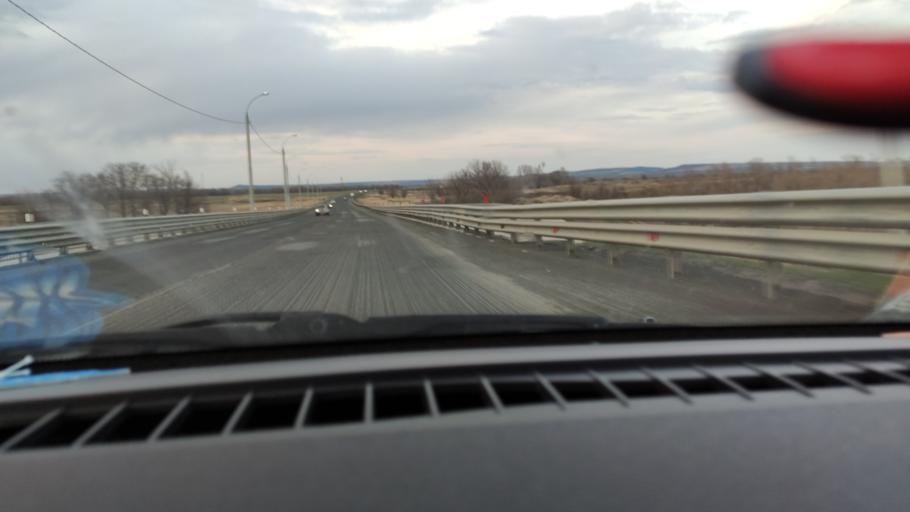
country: RU
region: Saratov
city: Yelshanka
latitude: 51.8082
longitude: 46.1972
